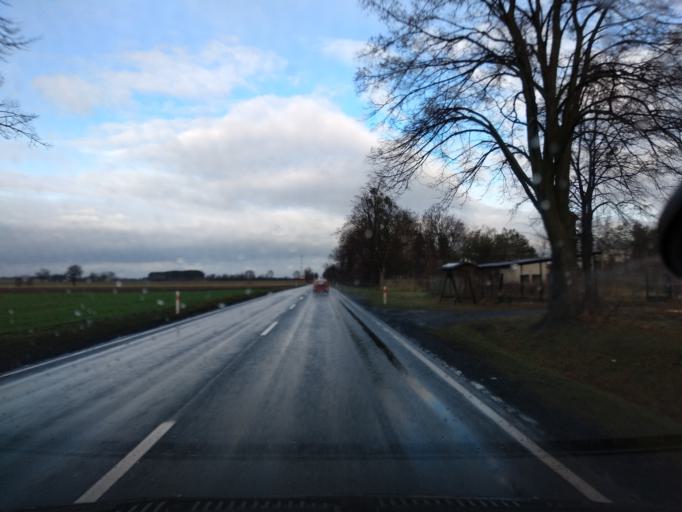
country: PL
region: Greater Poland Voivodeship
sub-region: Powiat koninski
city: Rychwal
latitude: 52.0444
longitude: 18.1622
